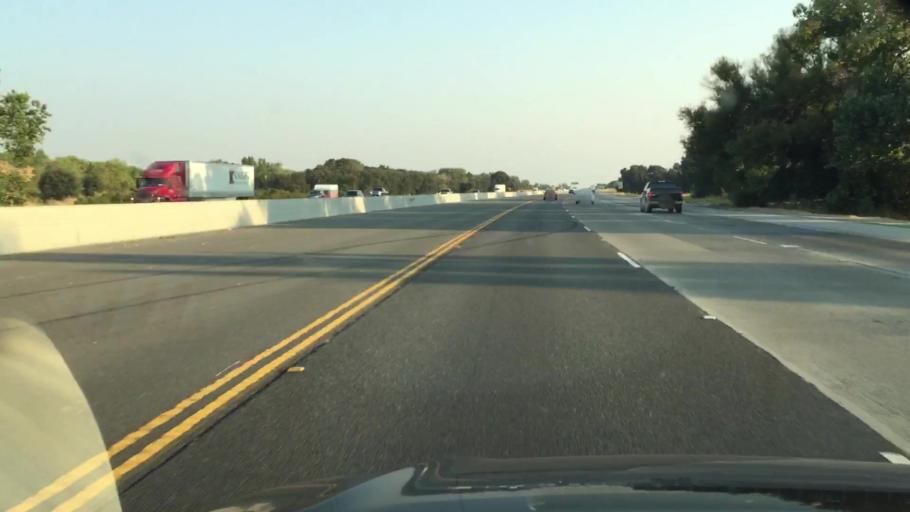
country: US
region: California
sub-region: Sacramento County
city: Parkway
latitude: 38.4560
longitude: -121.4938
